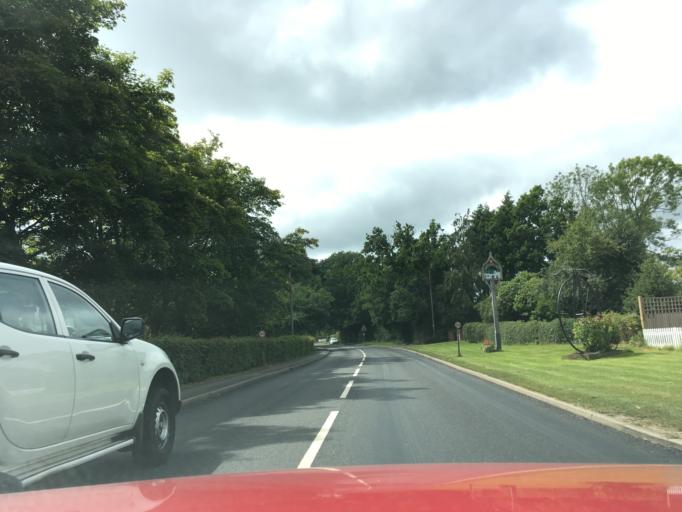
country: GB
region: England
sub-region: Kent
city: Cranbrook
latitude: 51.1091
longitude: 0.5585
